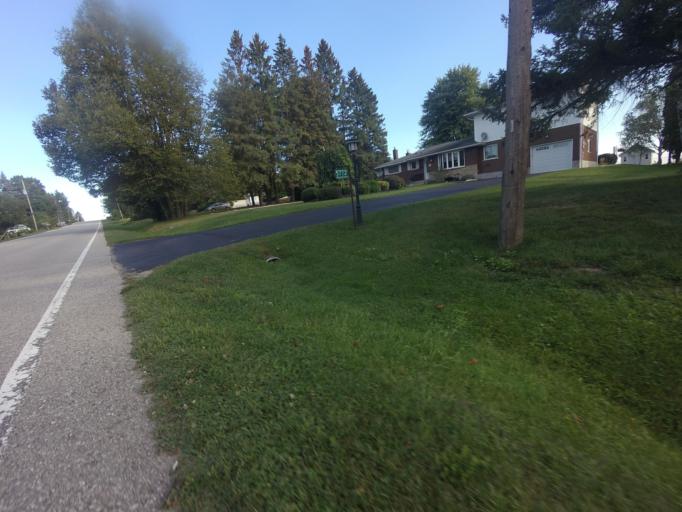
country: CA
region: Ontario
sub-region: Wellington County
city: Guelph
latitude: 43.5994
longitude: -80.3449
